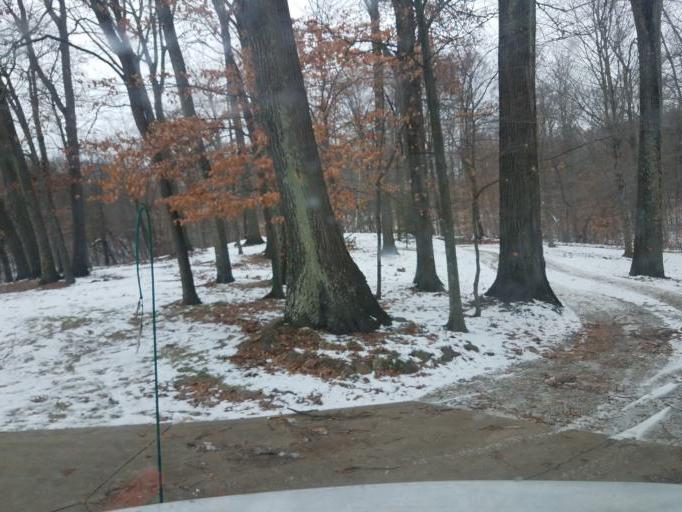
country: US
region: Ohio
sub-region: Richland County
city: Lincoln Heights
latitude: 40.6820
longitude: -82.4023
